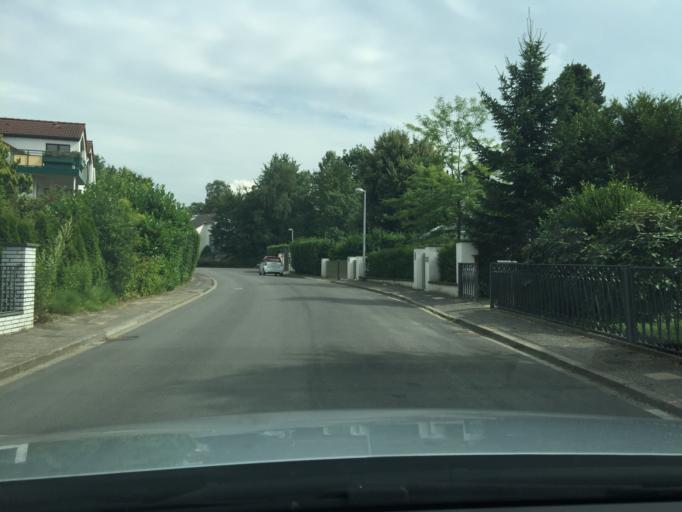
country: DE
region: North Rhine-Westphalia
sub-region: Regierungsbezirk Dusseldorf
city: Ratingen
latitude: 51.3379
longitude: 6.8945
